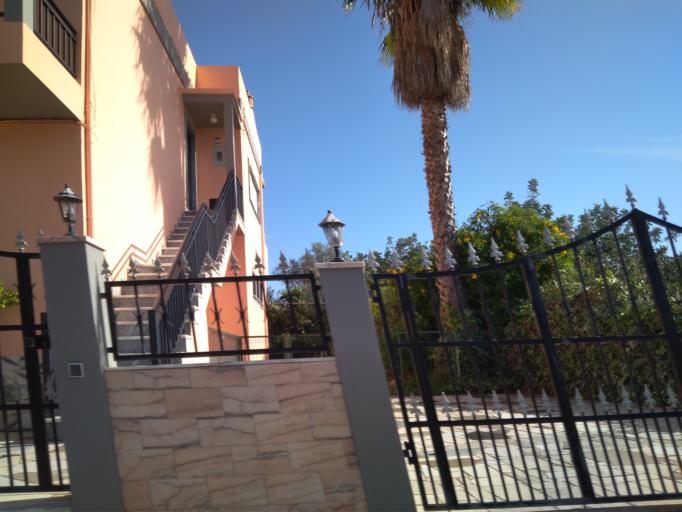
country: PT
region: Faro
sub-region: Faro
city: Santa Barbara de Nexe
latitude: 37.0853
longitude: -7.9586
